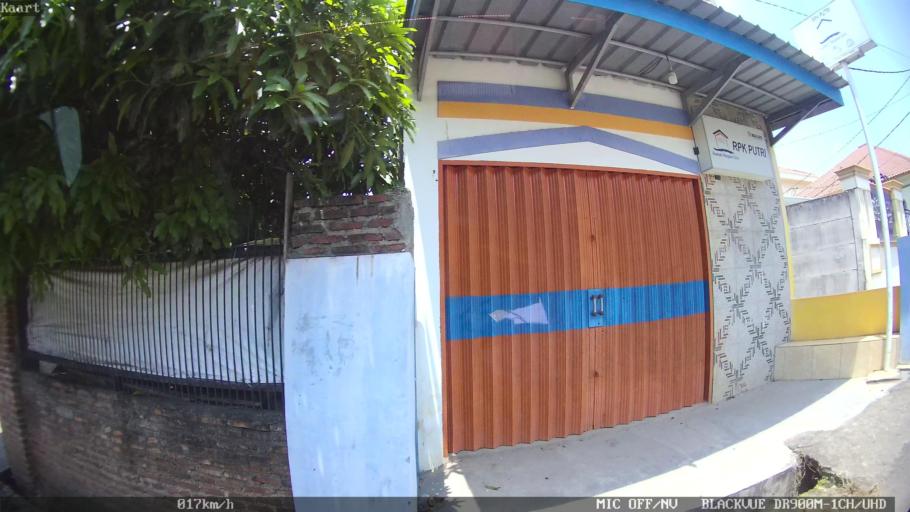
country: ID
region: Lampung
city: Kedaton
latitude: -5.3691
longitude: 105.2610
